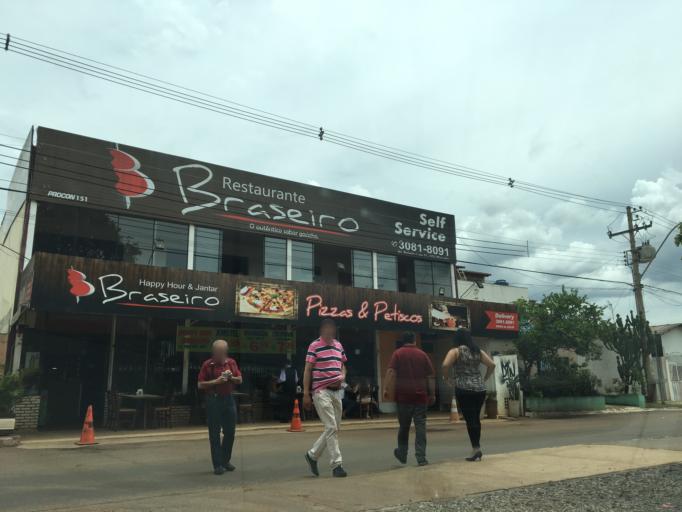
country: BR
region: Federal District
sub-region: Brasilia
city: Brasilia
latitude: -15.7966
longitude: -47.8518
